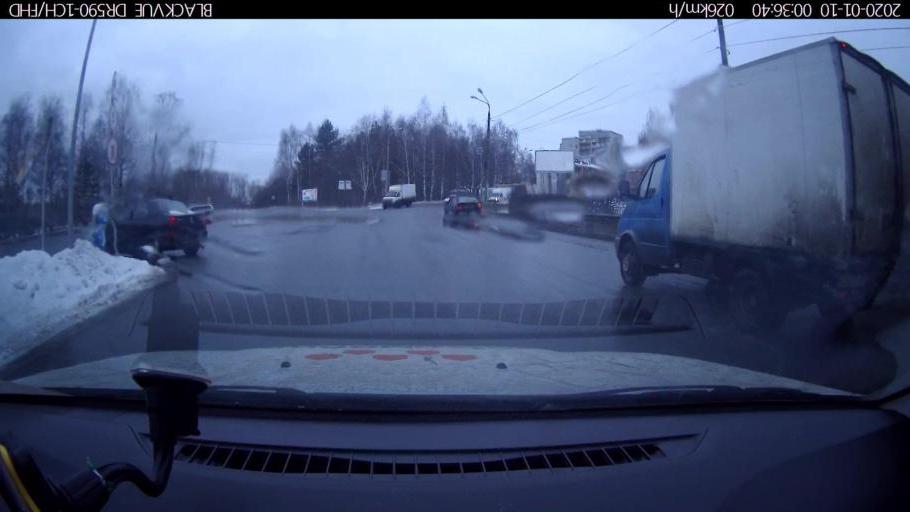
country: RU
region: Nizjnij Novgorod
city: Gorbatovka
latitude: 56.3147
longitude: 43.8658
